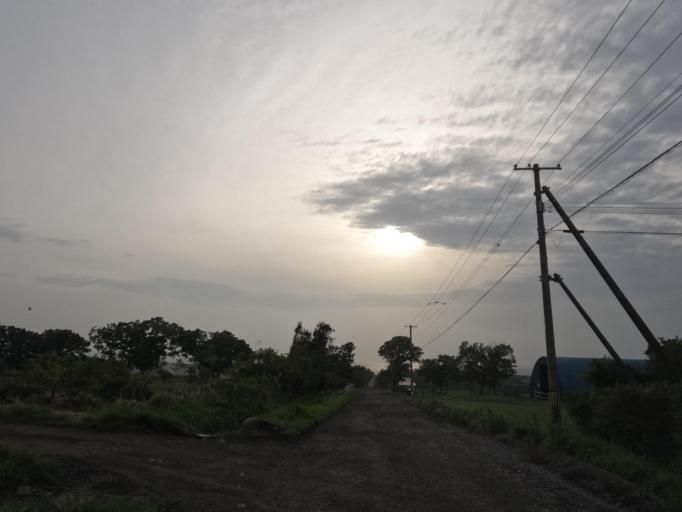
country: JP
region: Hokkaido
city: Date
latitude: 42.4242
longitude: 140.9162
